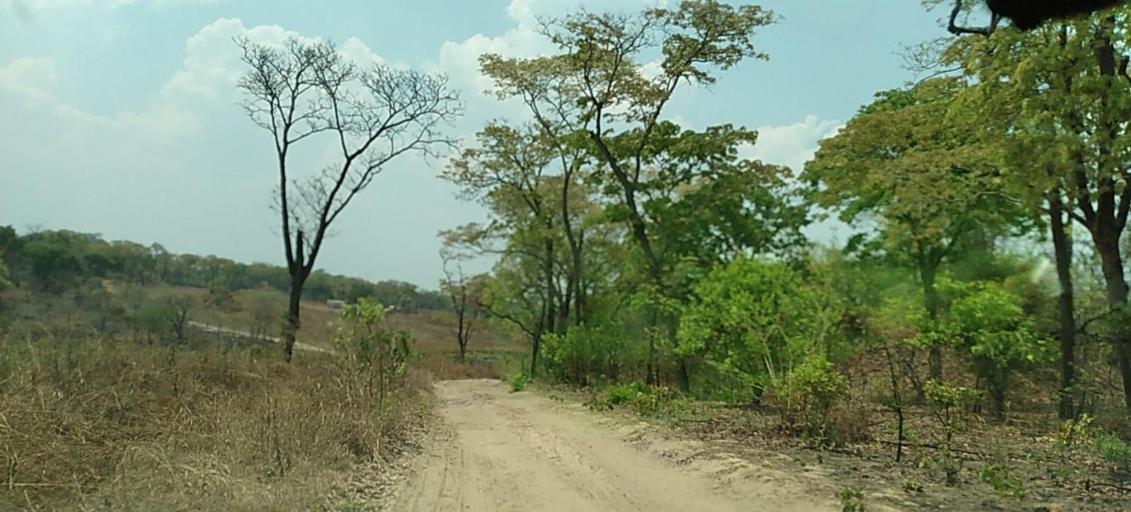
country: ZM
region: North-Western
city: Kabompo
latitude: -13.6358
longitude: 24.3849
